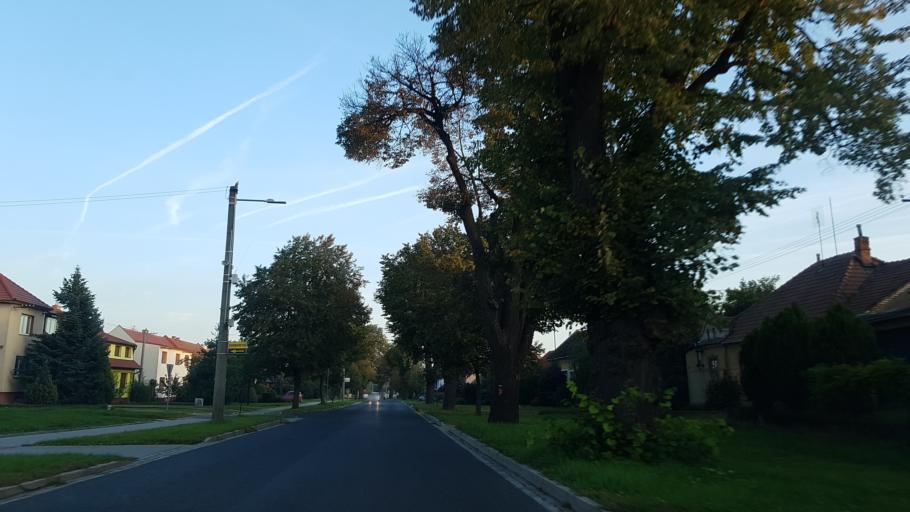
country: CZ
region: Zlin
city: Polesovice
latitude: 49.0269
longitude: 17.3523
